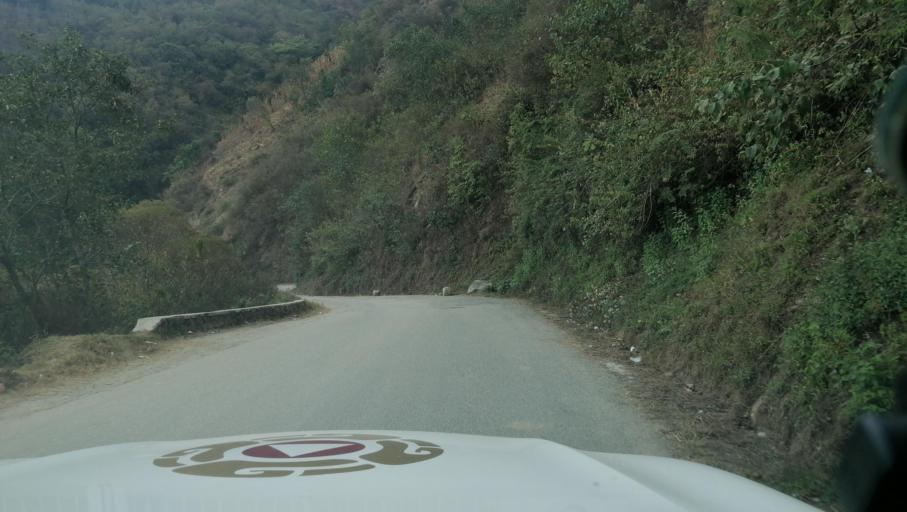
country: GT
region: San Marcos
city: Tacana
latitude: 15.2057
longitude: -92.1828
